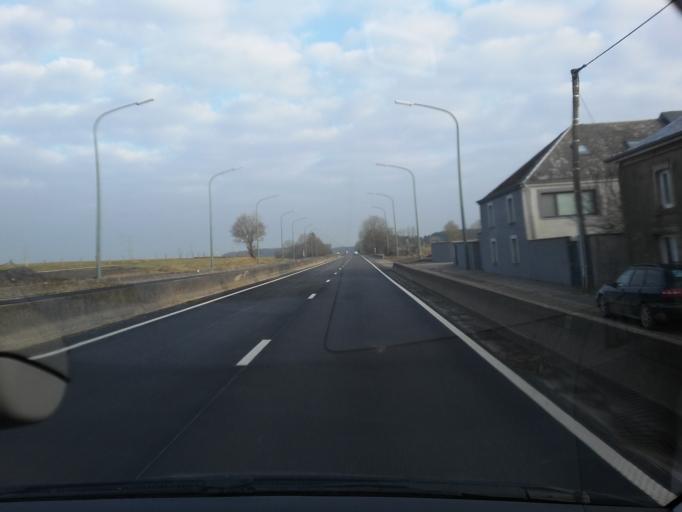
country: BE
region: Wallonia
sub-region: Province du Luxembourg
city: Martelange
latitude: 49.8679
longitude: 5.7128
